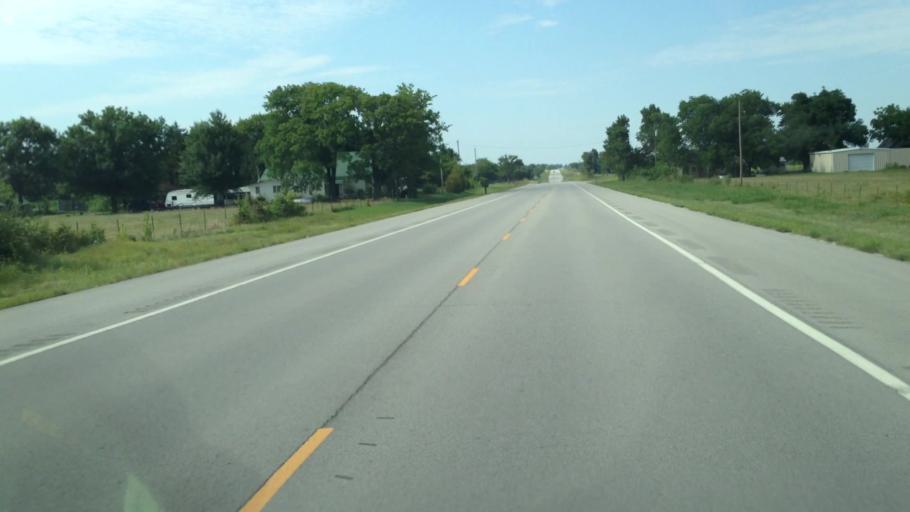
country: US
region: Kansas
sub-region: Labette County
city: Parsons
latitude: 37.2645
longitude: -95.2672
